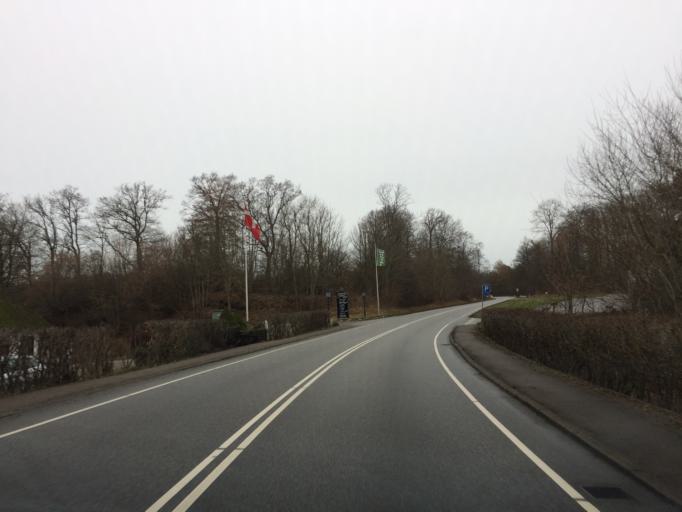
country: DK
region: Zealand
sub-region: Holbaek Kommune
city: Jyderup
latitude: 55.6119
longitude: 11.3872
